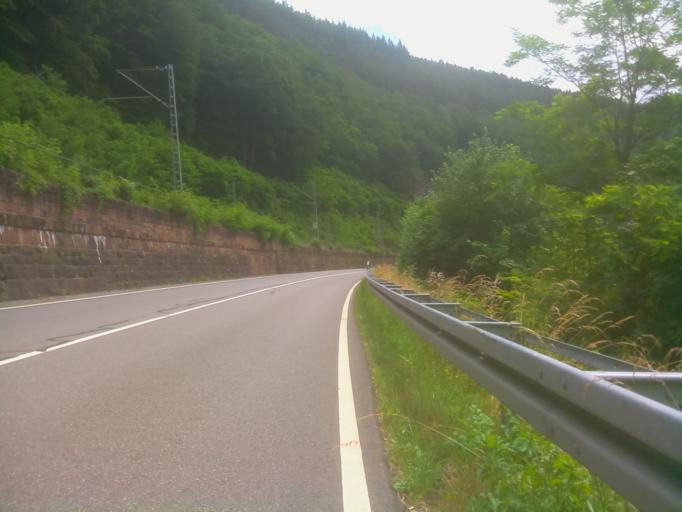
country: DE
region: Hesse
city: Hirschhorn
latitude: 49.4541
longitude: 8.9105
